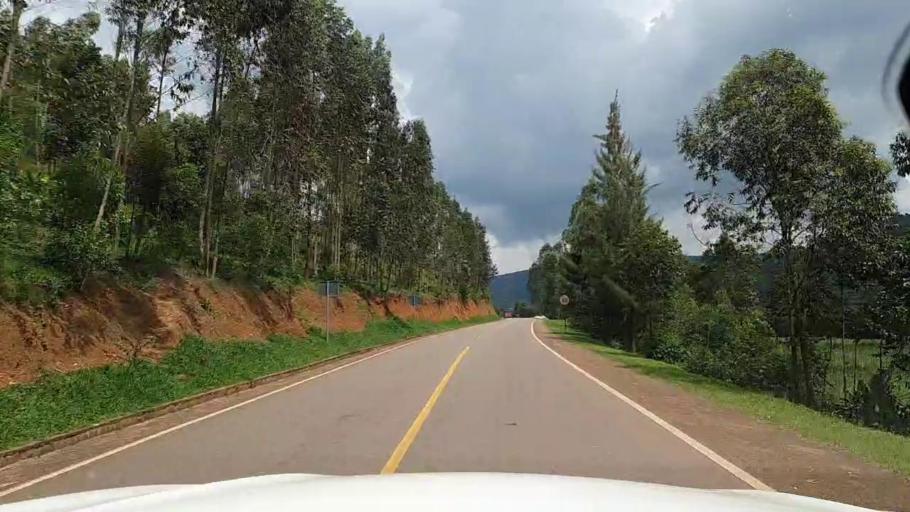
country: RW
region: Kigali
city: Kigali
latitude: -1.8015
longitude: 30.1284
